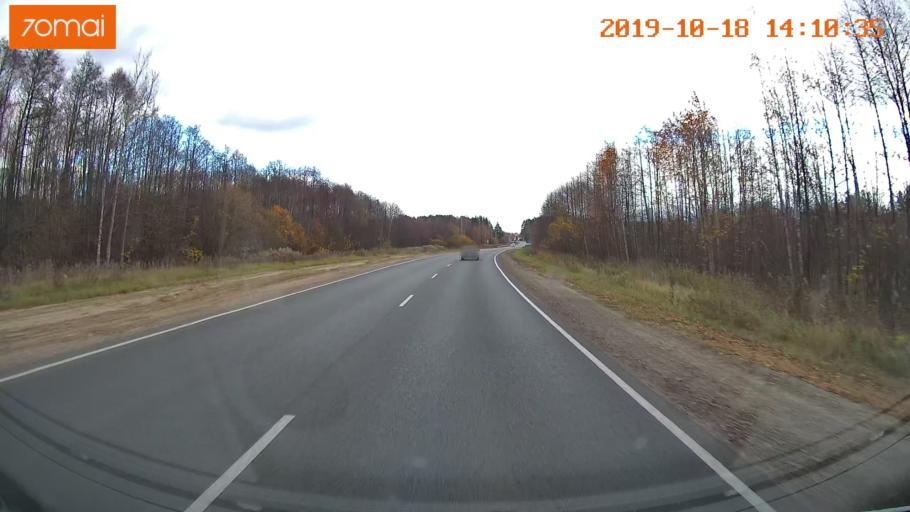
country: RU
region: Rjazan
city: Spas-Klepiki
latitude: 55.1414
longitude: 40.2114
